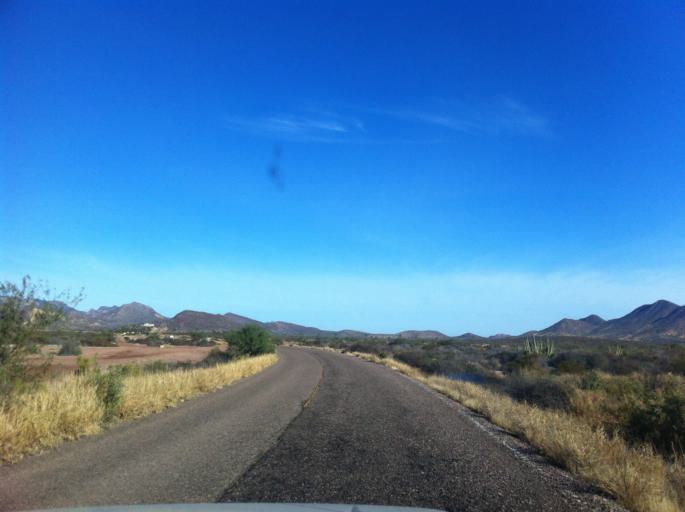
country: MX
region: Sonora
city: Heroica Guaymas
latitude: 27.9616
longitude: -110.9670
